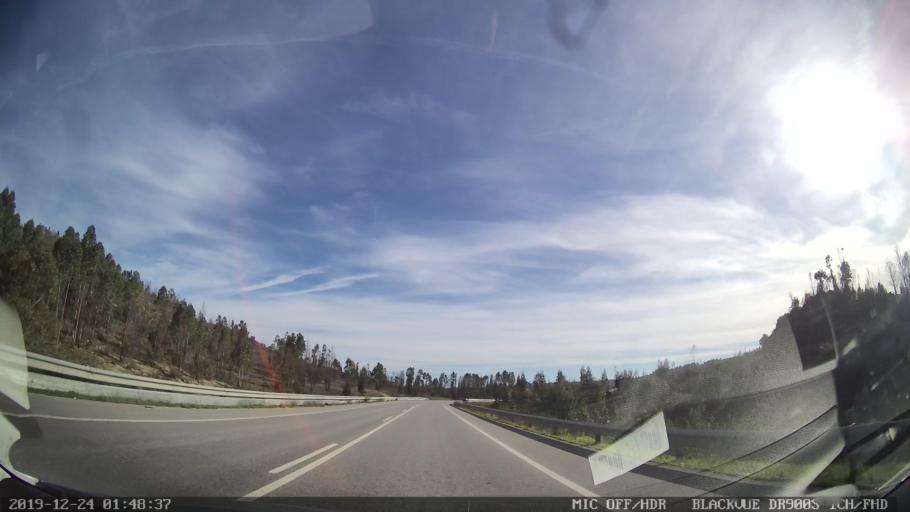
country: PT
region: Portalegre
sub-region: Nisa
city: Nisa
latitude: 39.5195
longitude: -7.7732
